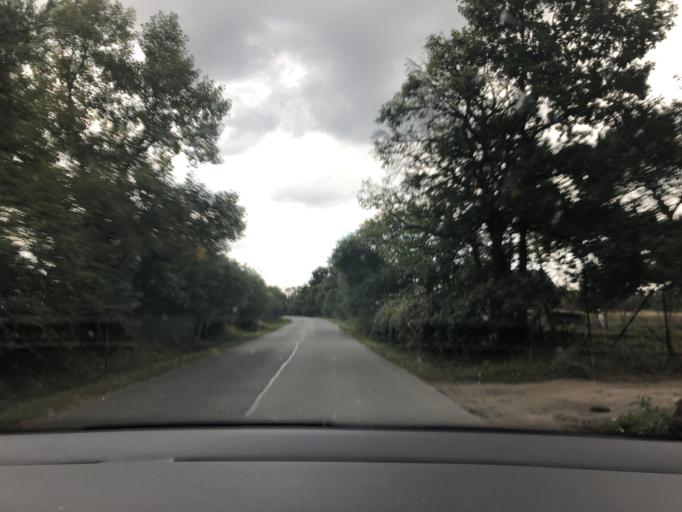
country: CZ
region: Central Bohemia
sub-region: Okres Kolin
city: Tynec nad Labem
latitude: 50.0325
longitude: 15.3532
